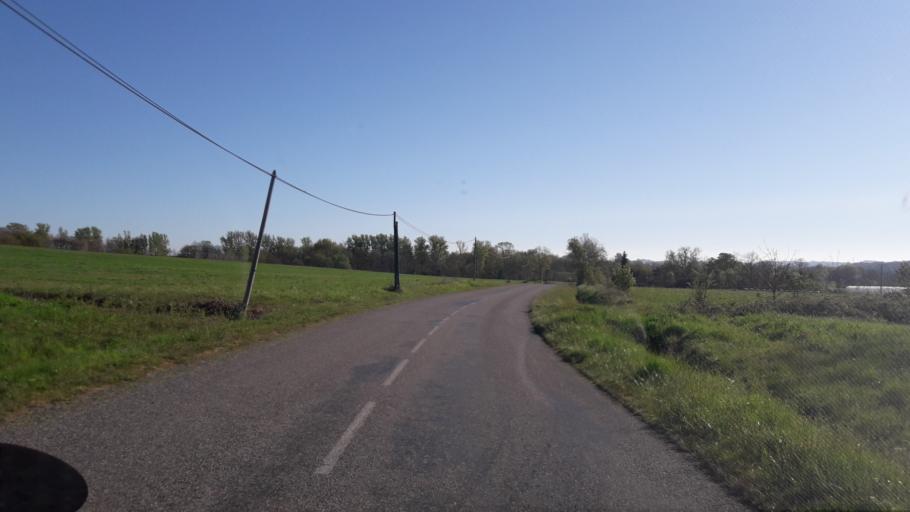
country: FR
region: Midi-Pyrenees
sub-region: Departement de la Haute-Garonne
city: Rieux-Volvestre
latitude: 43.2001
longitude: 1.1555
